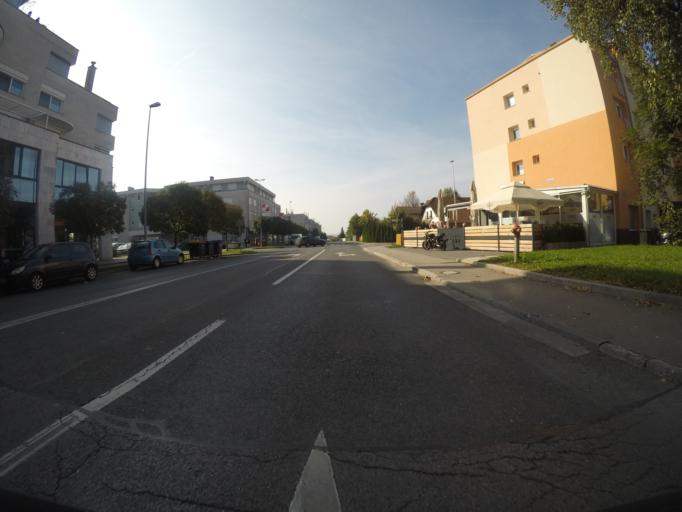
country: SI
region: Kamnik
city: Kamnik
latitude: 46.2192
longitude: 14.6049
